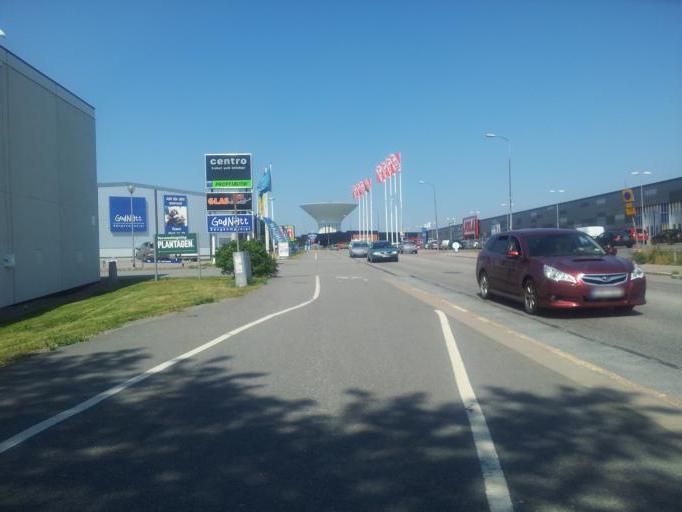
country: SE
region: Uppsala
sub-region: Uppsala Kommun
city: Saevja
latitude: 59.8517
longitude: 17.6876
